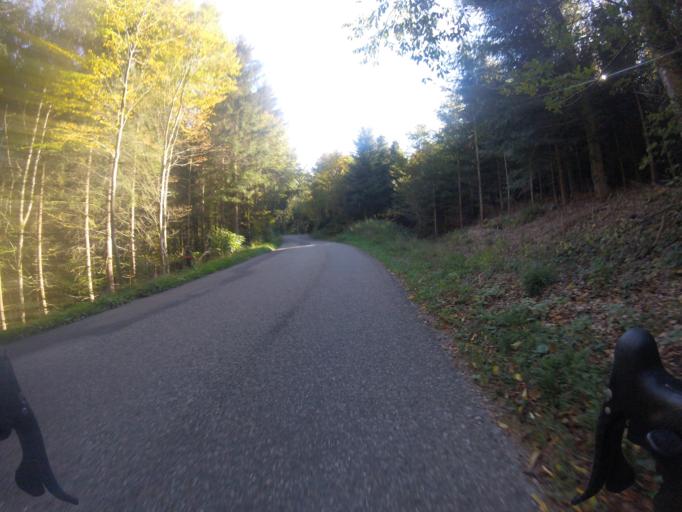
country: CH
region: Bern
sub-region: Seeland District
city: Schupfen
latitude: 47.0312
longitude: 7.3916
